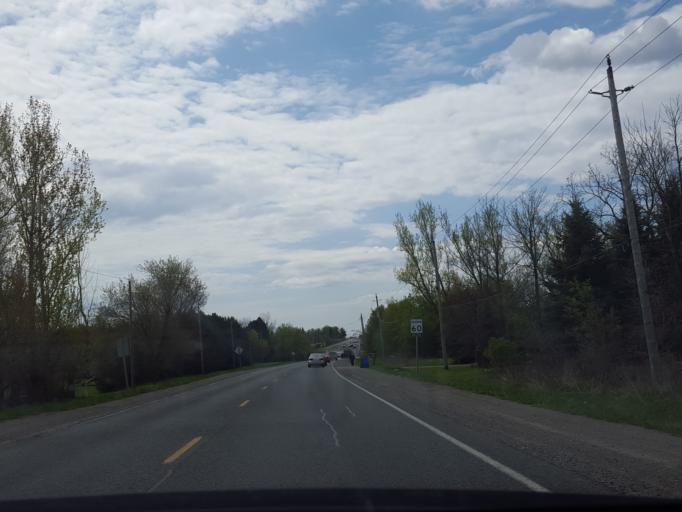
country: CA
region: Ontario
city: Oshawa
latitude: 43.9169
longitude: -78.7043
